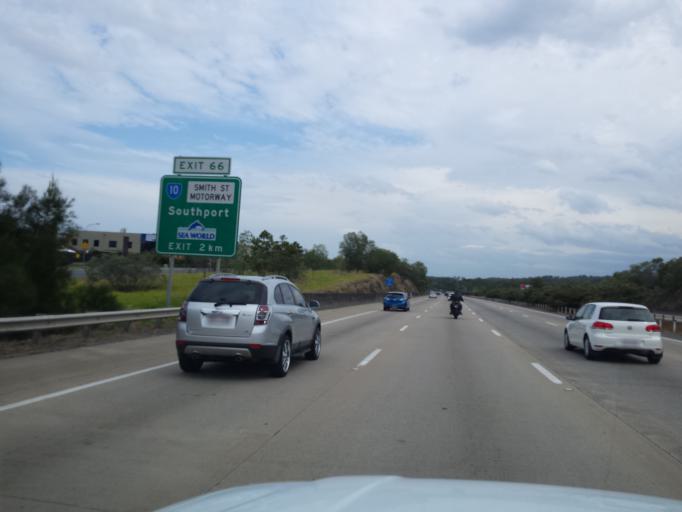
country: AU
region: Queensland
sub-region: Gold Coast
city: Upper Coomera
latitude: -27.9352
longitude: 153.3356
